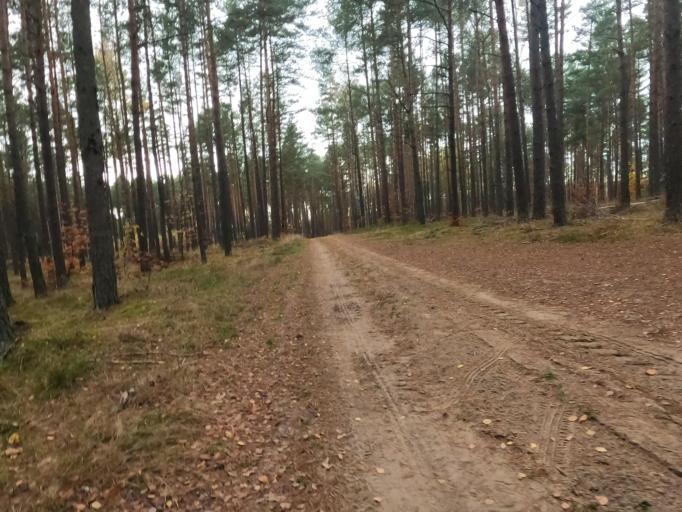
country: PL
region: Pomeranian Voivodeship
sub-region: Powiat starogardzki
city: Skarszewy
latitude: 54.0507
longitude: 18.4459
